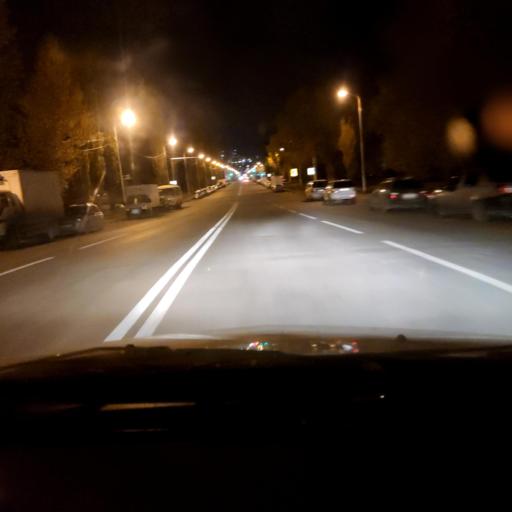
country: RU
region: Bashkortostan
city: Ufa
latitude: 54.7734
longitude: 56.0848
